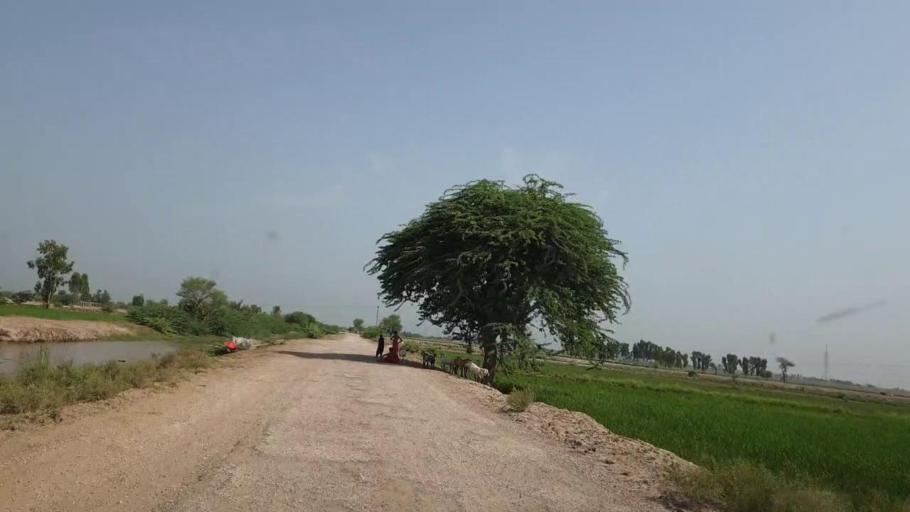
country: PK
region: Sindh
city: Lakhi
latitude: 27.8252
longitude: 68.6882
